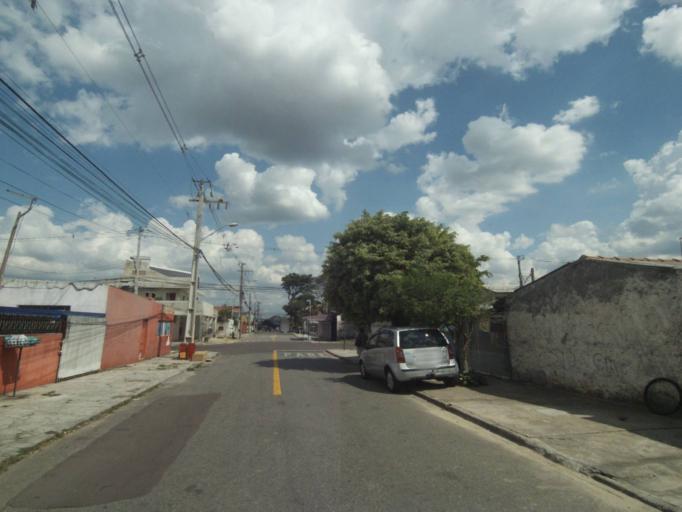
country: BR
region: Parana
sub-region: Sao Jose Dos Pinhais
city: Sao Jose dos Pinhais
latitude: -25.5338
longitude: -49.2606
